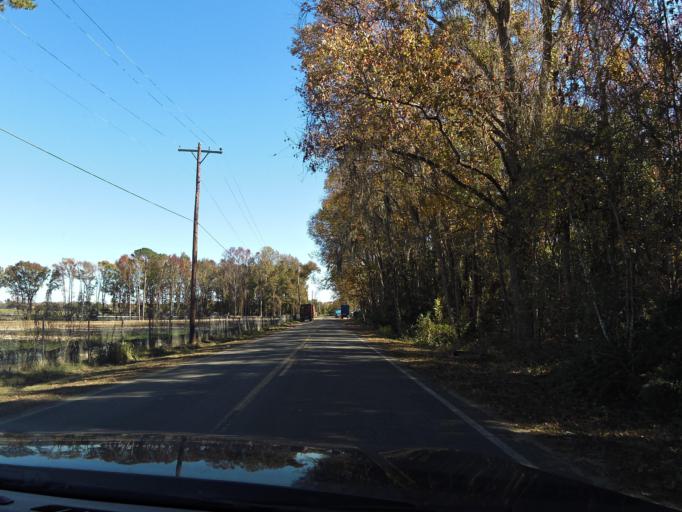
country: US
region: Georgia
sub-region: Chatham County
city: Savannah
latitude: 32.0642
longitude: -81.1423
